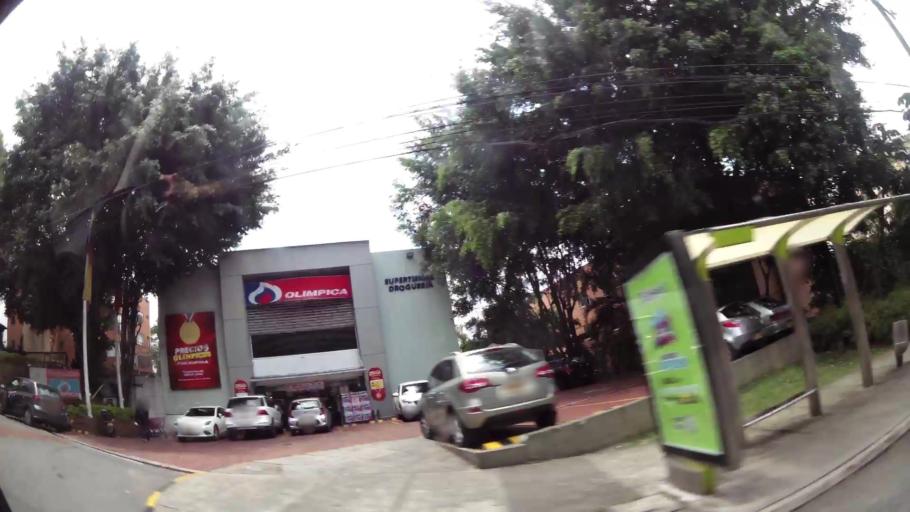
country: CO
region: Antioquia
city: Envigado
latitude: 6.1831
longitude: -75.5706
